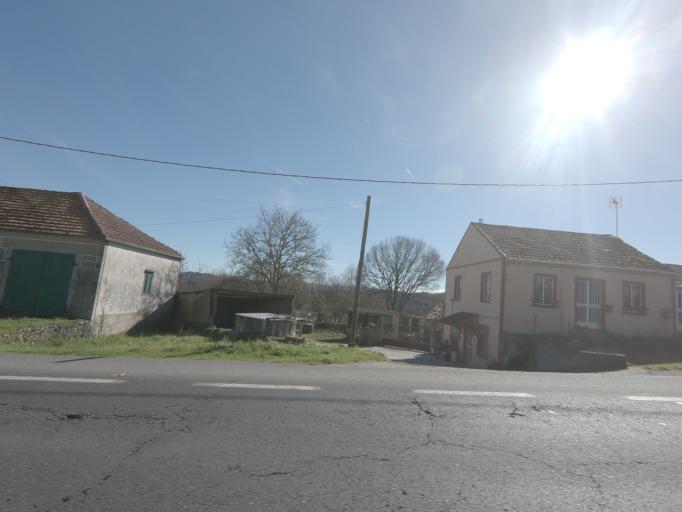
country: ES
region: Galicia
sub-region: Provincia de Pontevedra
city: Silleda
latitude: 42.6860
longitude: -8.2159
